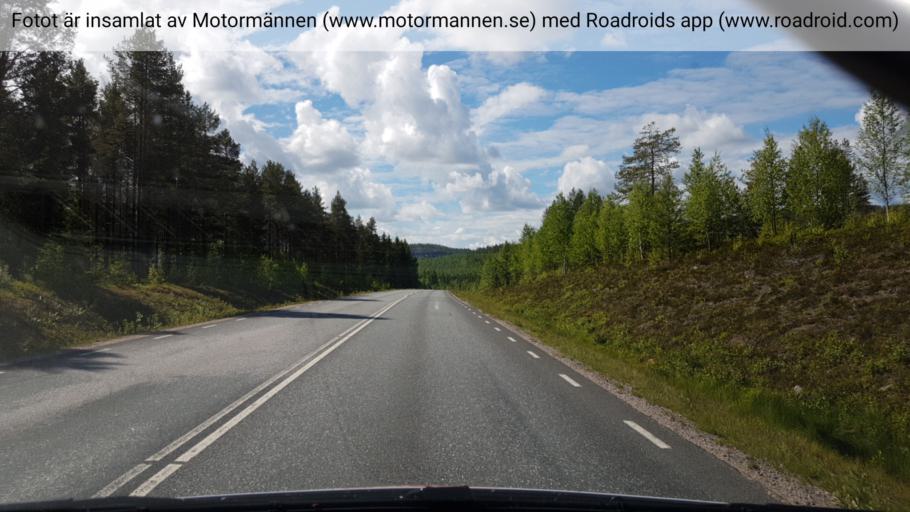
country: FI
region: Lapland
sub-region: Torniolaakso
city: Ylitornio
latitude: 66.3318
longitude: 23.6367
